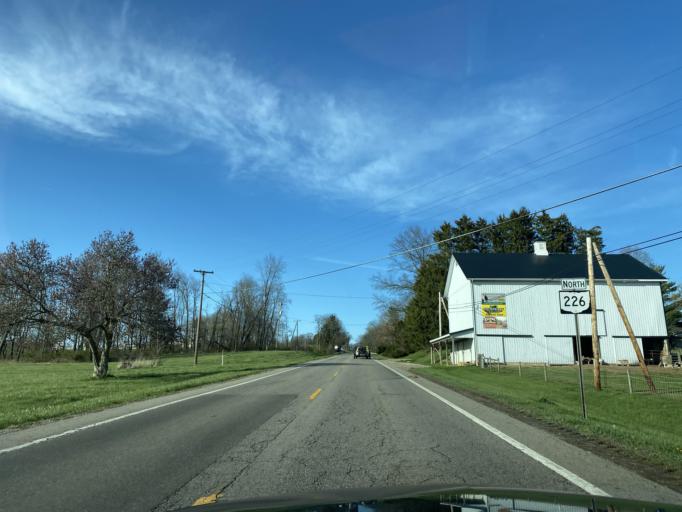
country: US
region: Ohio
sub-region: Wayne County
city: Wooster
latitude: 40.7554
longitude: -81.9783
